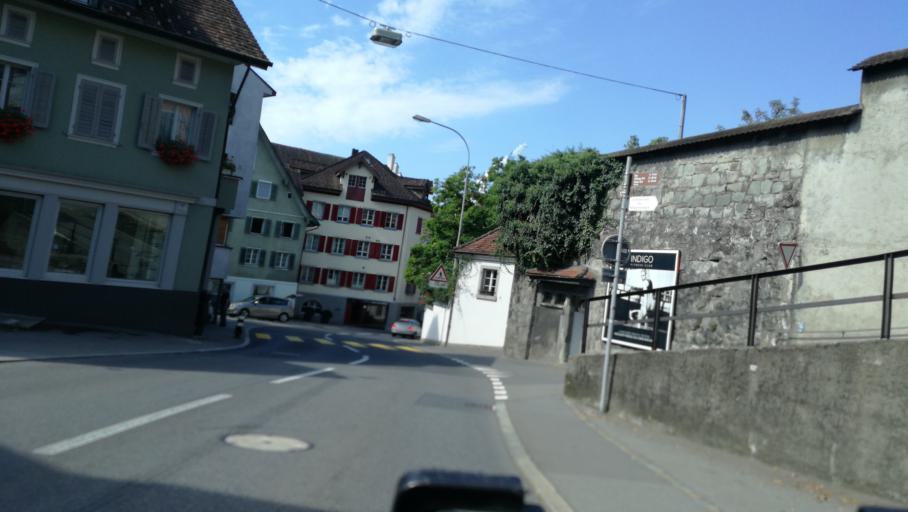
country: CH
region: Zug
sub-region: Zug
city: Zug
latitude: 47.1663
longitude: 8.5179
